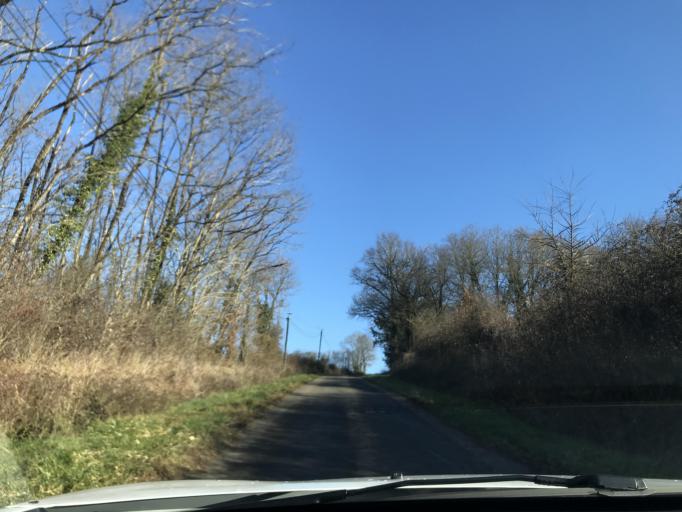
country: FR
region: Poitou-Charentes
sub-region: Departement de la Charente
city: Chasseneuil-sur-Bonnieure
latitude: 45.8453
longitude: 0.5122
